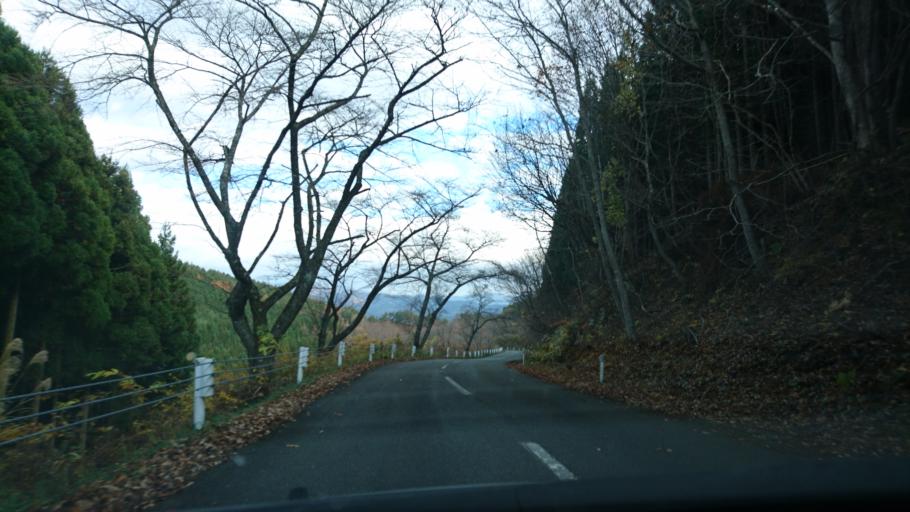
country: JP
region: Iwate
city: Ichinoseki
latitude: 39.0231
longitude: 141.1803
